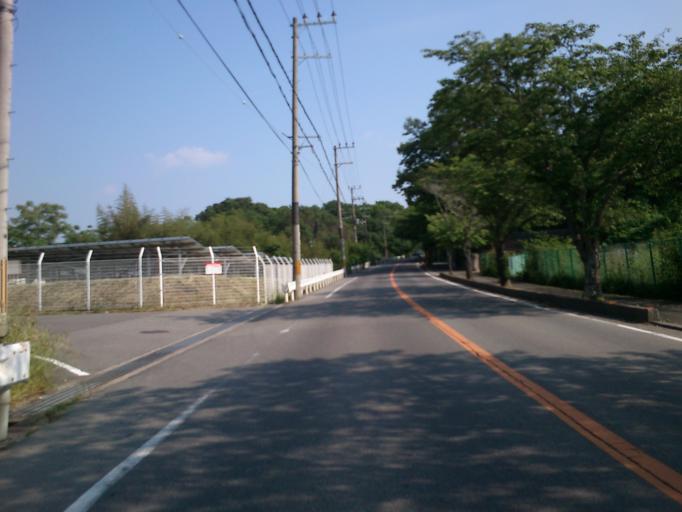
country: JP
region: Kyoto
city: Kameoka
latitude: 35.0486
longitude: 135.5750
